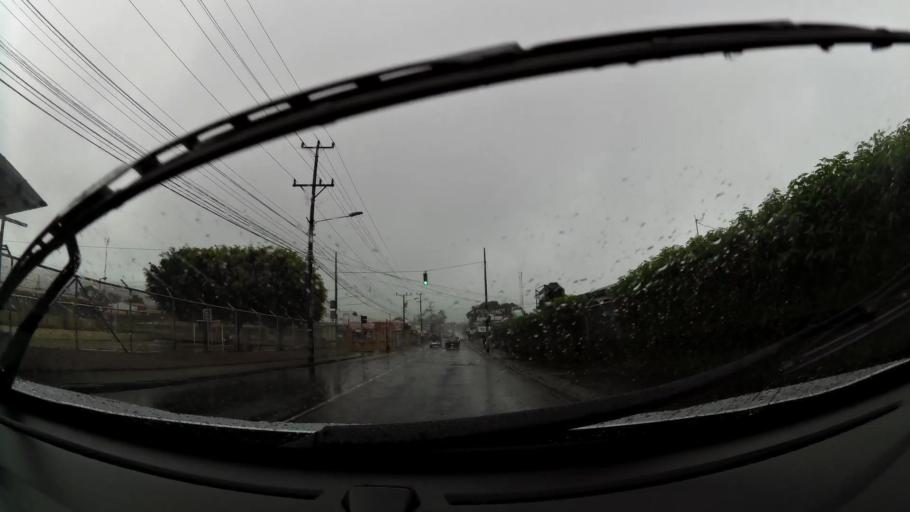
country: CR
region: Cartago
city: Cartago
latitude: 9.8621
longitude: -83.9140
